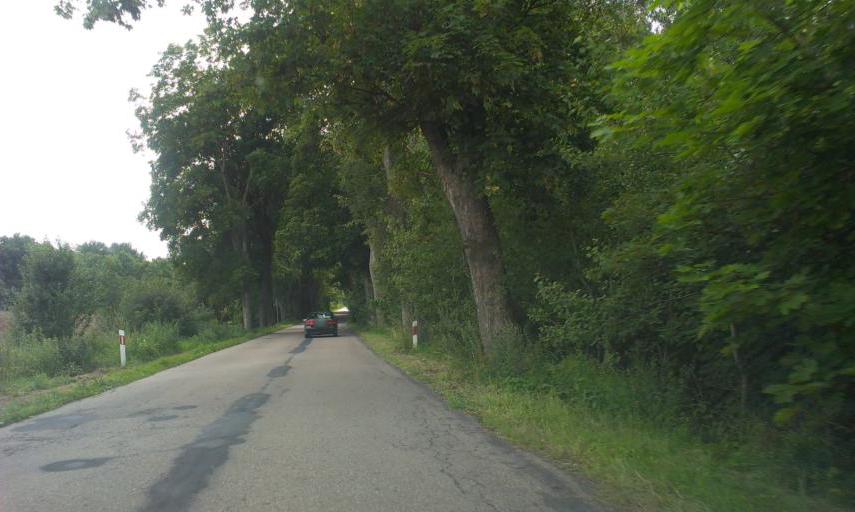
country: PL
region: West Pomeranian Voivodeship
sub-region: Powiat szczecinecki
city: Barwice
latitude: 53.7047
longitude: 16.3522
